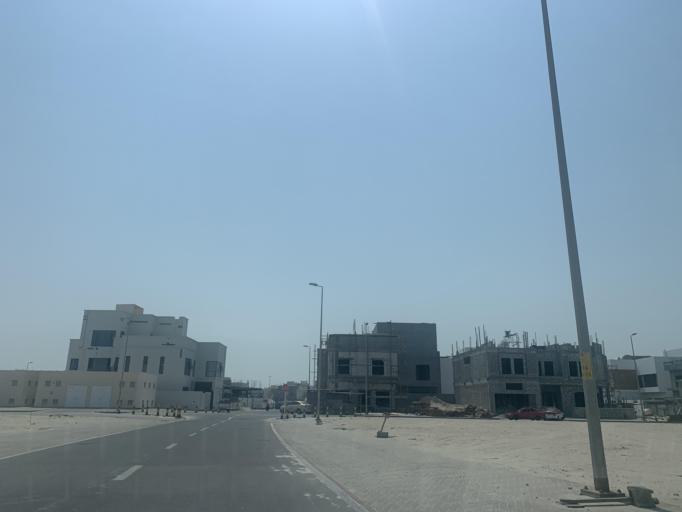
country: BH
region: Muharraq
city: Al Hadd
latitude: 26.2358
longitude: 50.6610
